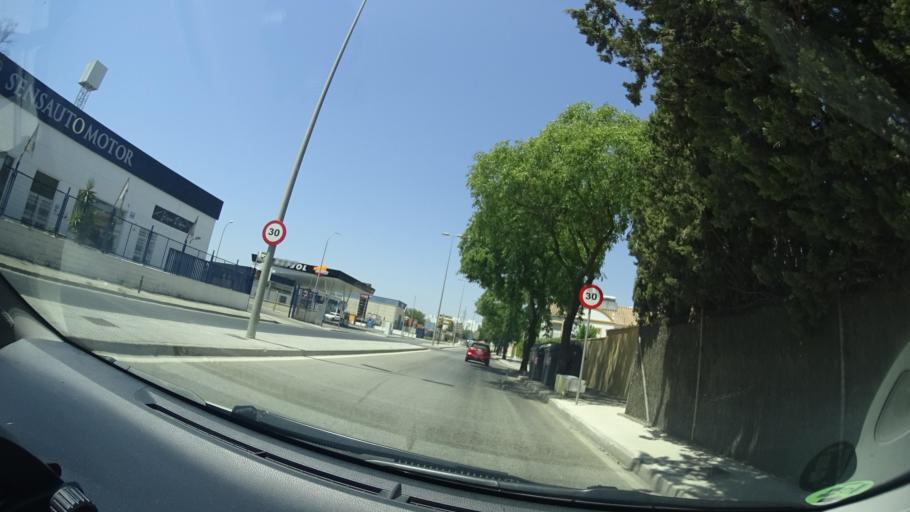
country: ES
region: Andalusia
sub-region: Provincia de Cadiz
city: Jerez de la Frontera
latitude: 36.6708
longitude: -6.1213
